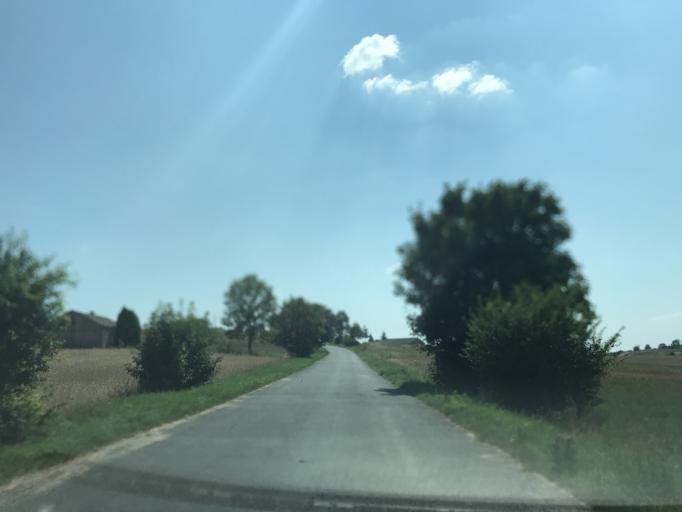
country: PL
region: Kujawsko-Pomorskie
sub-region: Powiat lipnowski
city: Chrostkowo
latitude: 52.9484
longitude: 19.2173
